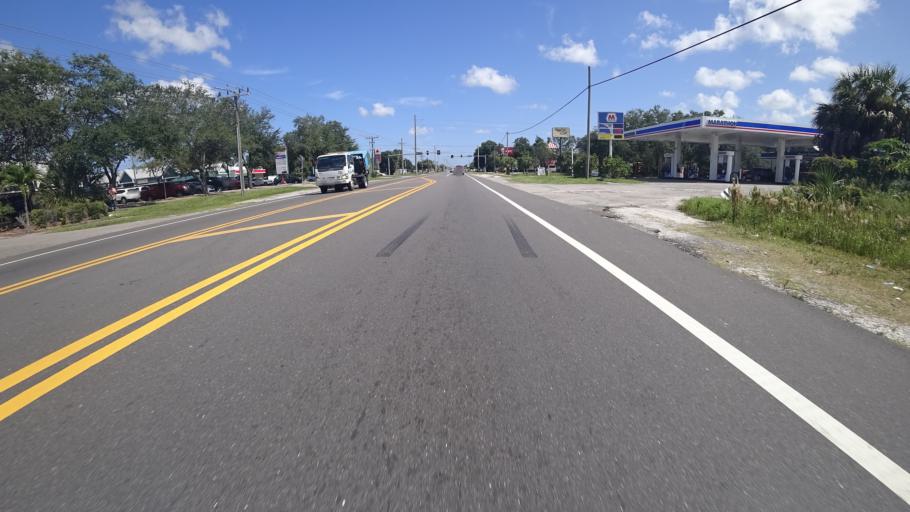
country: US
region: Florida
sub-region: Manatee County
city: Whitfield
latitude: 27.4281
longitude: -82.5467
